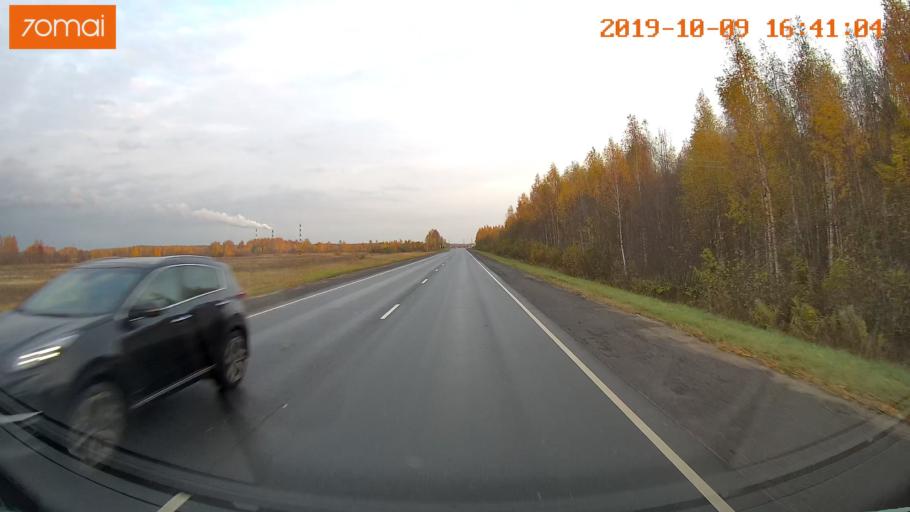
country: RU
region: Kostroma
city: Volgorechensk
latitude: 57.4766
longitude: 41.0730
